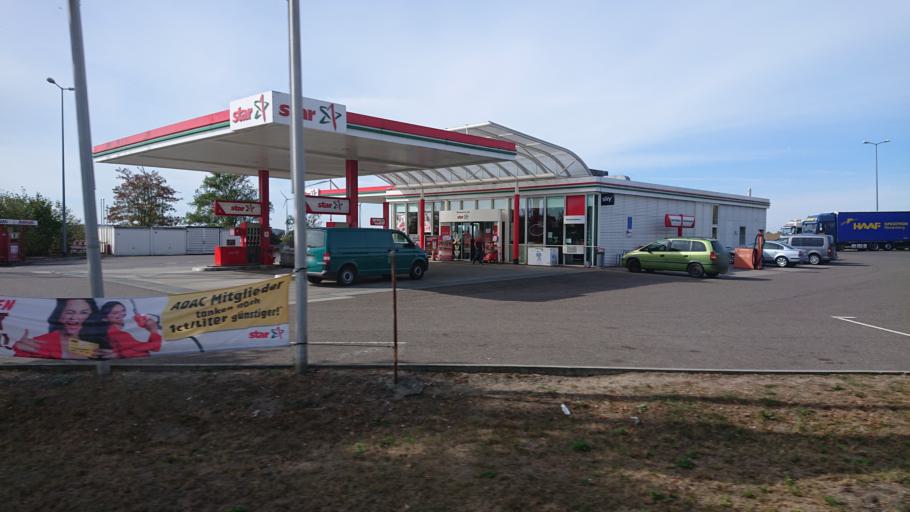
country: DE
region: Brandenburg
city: Gramzow
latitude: 53.2349
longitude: 13.9864
